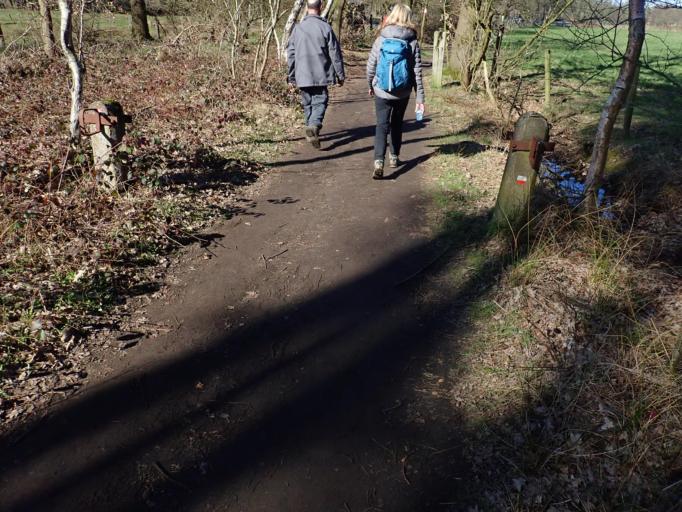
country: BE
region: Flanders
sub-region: Provincie Vlaams-Brabant
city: Scherpenheuvel-Zichem
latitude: 51.0463
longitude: 4.9823
